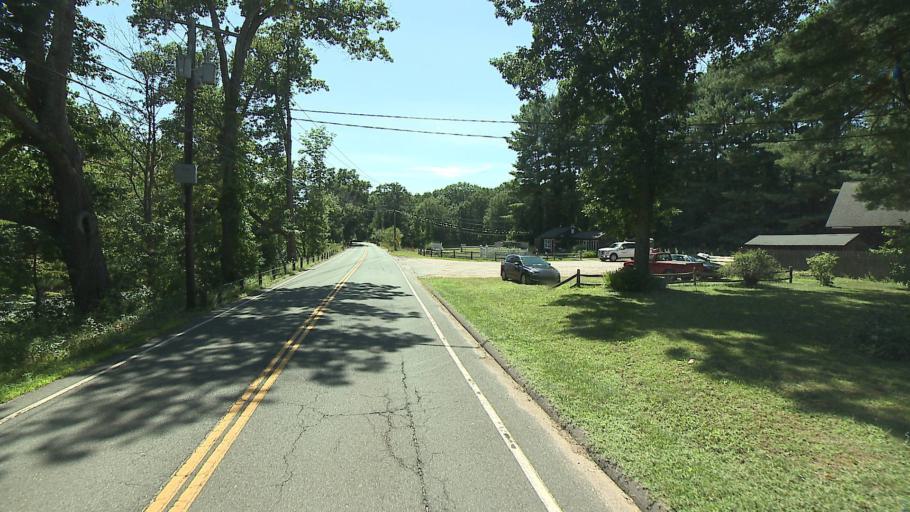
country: US
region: Connecticut
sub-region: Litchfield County
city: New Hartford Center
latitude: 41.9074
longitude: -72.9882
